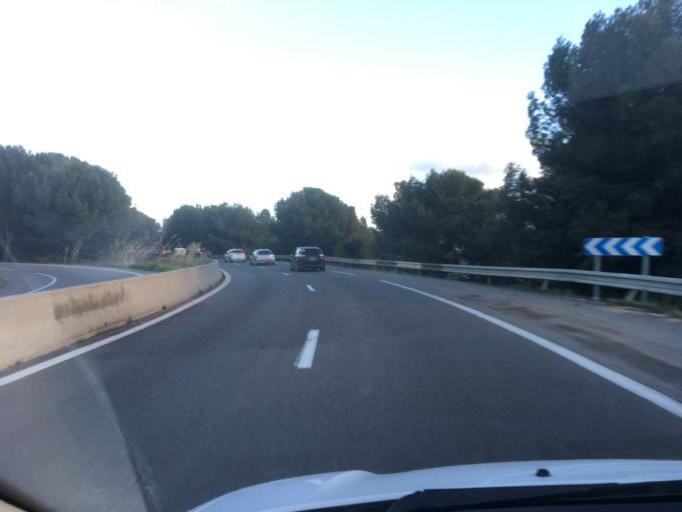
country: FR
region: Provence-Alpes-Cote d'Azur
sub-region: Departement des Bouches-du-Rhone
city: Martigues
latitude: 43.4072
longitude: 5.0363
